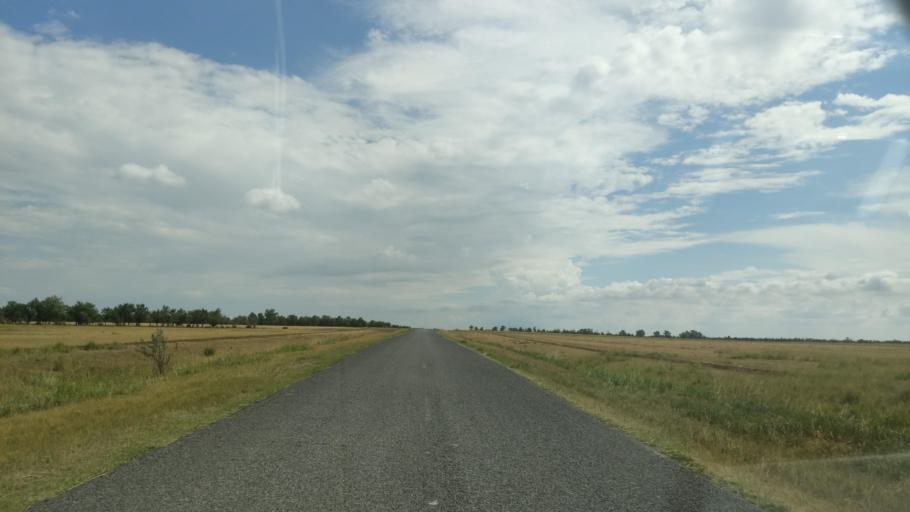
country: KZ
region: Pavlodar
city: Pavlodar
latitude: 52.6366
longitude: 76.9589
